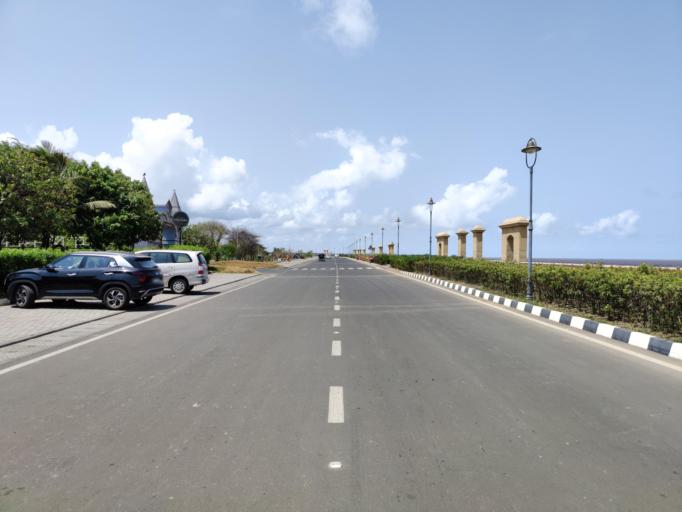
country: IN
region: Daman and Diu
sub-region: Daman District
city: Daman
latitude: 20.4074
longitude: 72.8290
